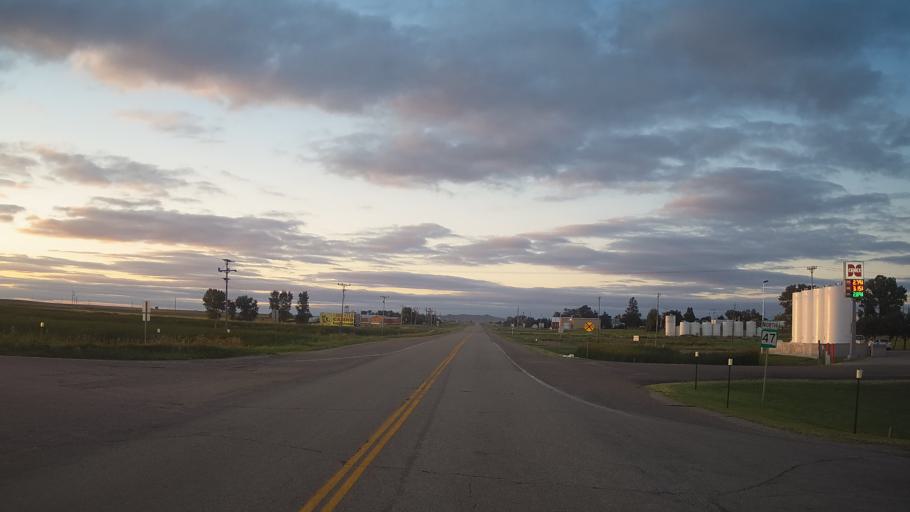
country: US
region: South Dakota
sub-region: Buffalo County
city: Fort Thompson
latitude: 43.8752
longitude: -99.6059
